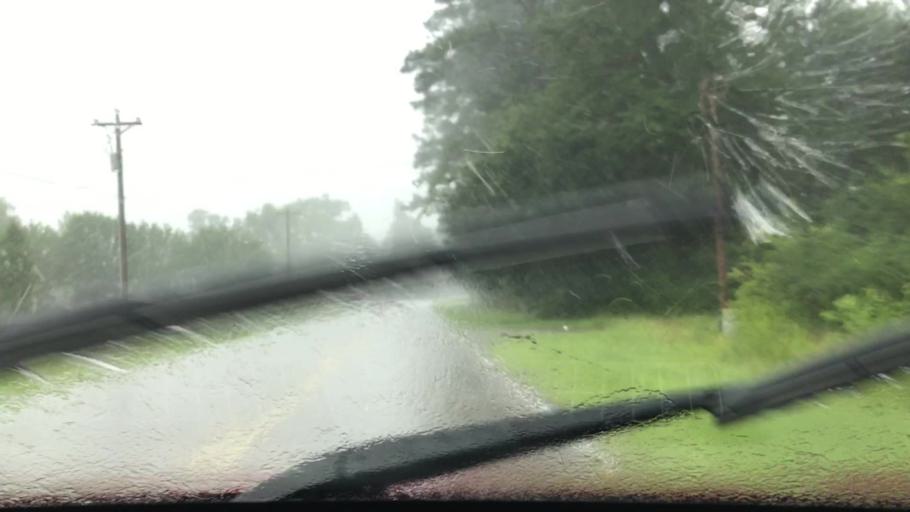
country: US
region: South Carolina
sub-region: Horry County
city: Red Hill
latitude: 33.8842
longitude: -78.9636
